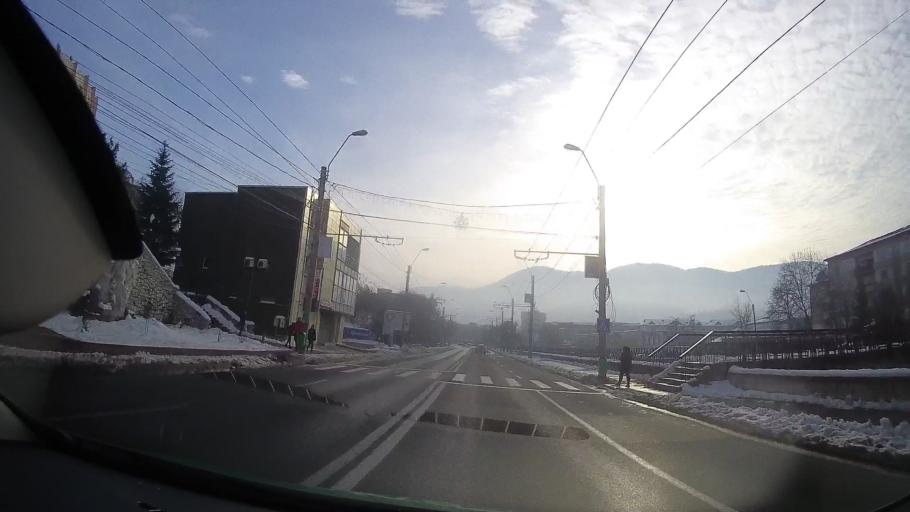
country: RO
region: Neamt
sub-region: Municipiul Piatra-Neamt
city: Valeni
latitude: 46.9289
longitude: 26.3727
